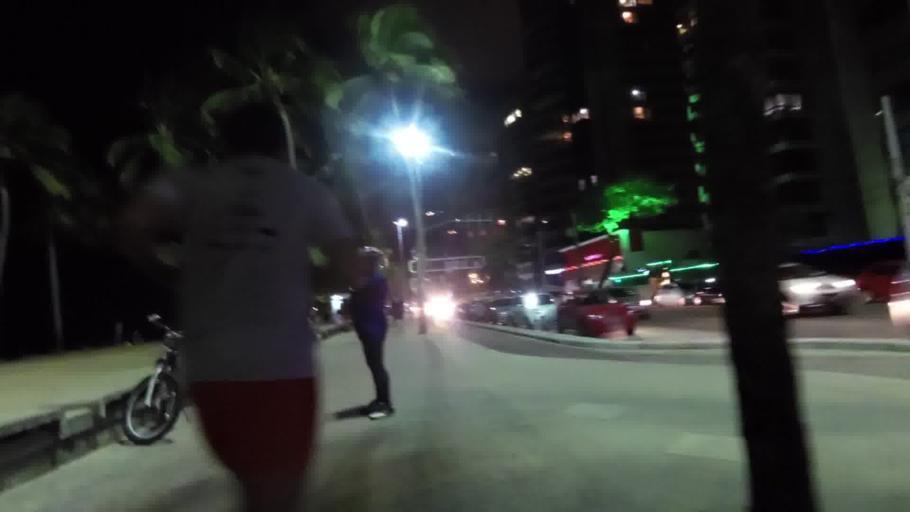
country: BR
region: Pernambuco
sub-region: Recife
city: Recife
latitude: -8.1148
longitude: -34.8917
